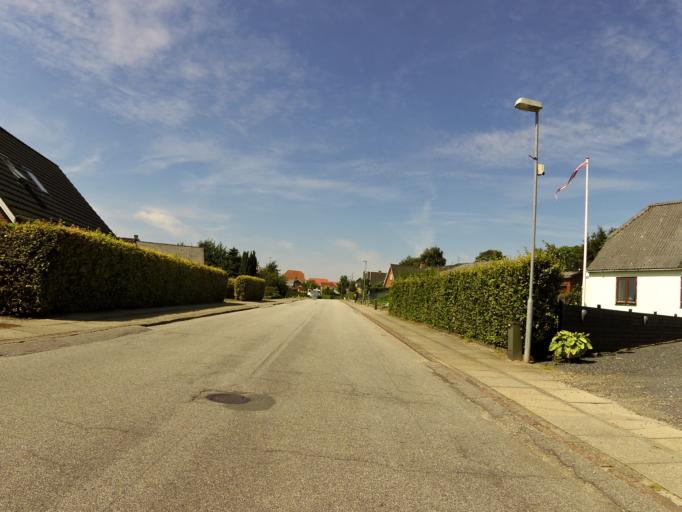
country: DK
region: South Denmark
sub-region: Haderslev Kommune
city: Gram
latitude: 55.2460
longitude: 8.9730
